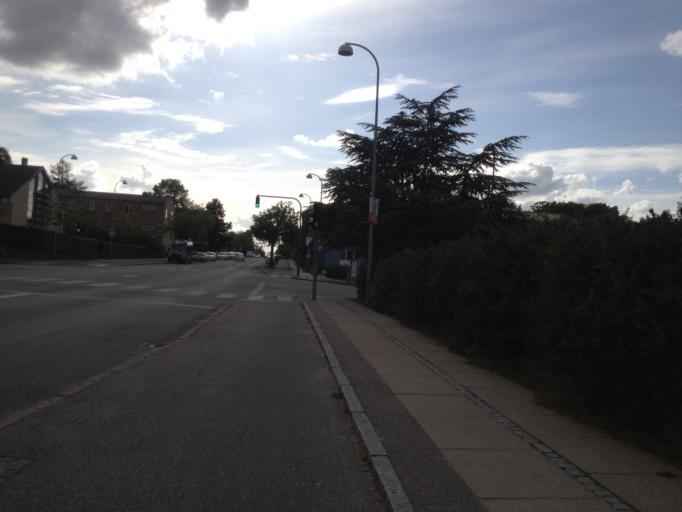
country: DK
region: Capital Region
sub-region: Gladsaxe Municipality
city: Buddinge
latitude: 55.7421
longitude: 12.5071
